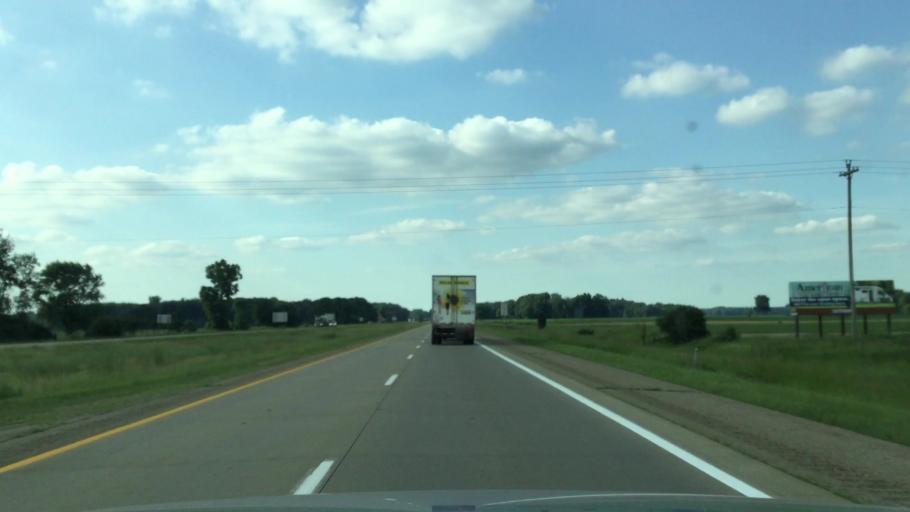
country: US
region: Michigan
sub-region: Branch County
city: Union City
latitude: 42.1157
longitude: -84.9953
